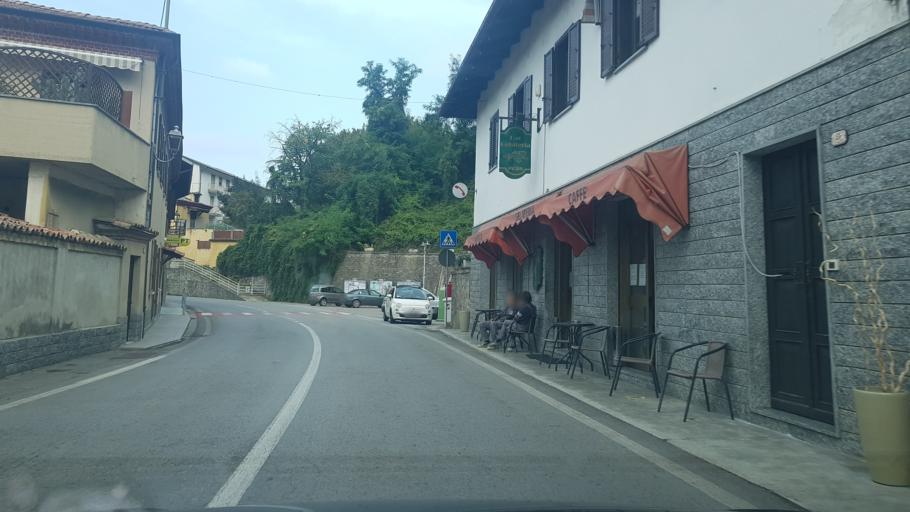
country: IT
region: Piedmont
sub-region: Provincia di Cuneo
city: Cossano Belbo
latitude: 44.6668
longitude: 8.1977
